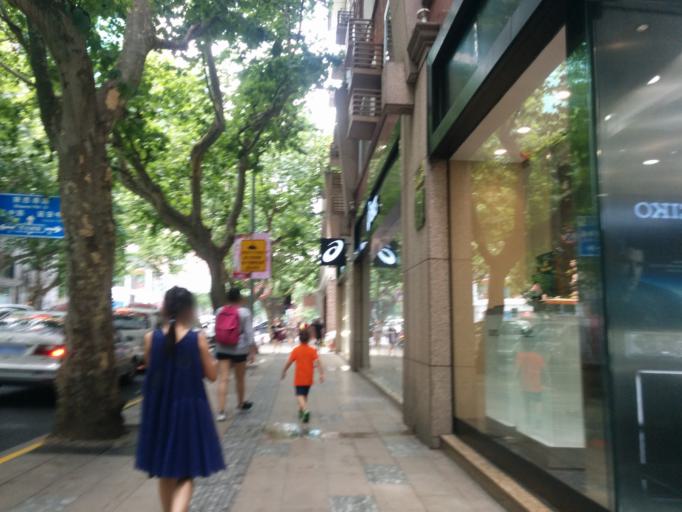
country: CN
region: Shanghai Shi
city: Shanghai
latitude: 31.2200
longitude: 121.4573
